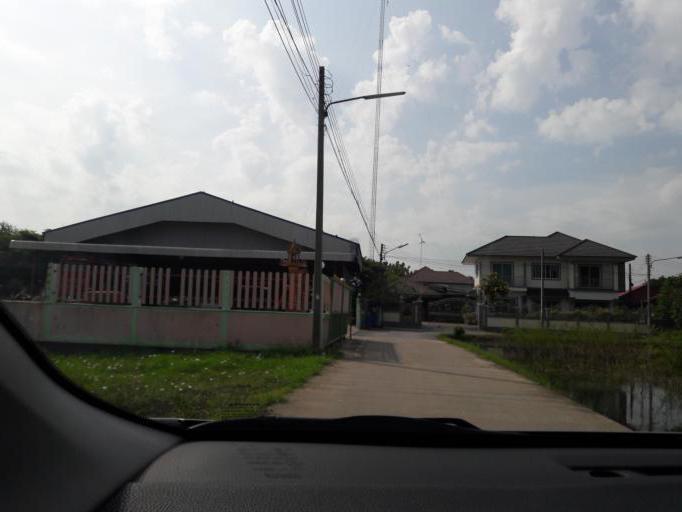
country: TH
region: Ang Thong
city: Ang Thong
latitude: 14.5983
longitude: 100.4350
